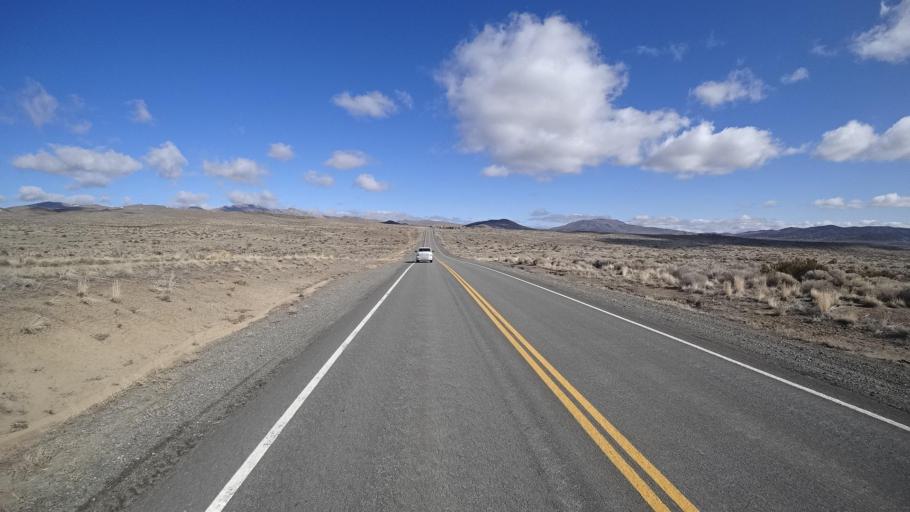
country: US
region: Nevada
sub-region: Washoe County
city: Cold Springs
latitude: 39.6741
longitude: -119.9225
